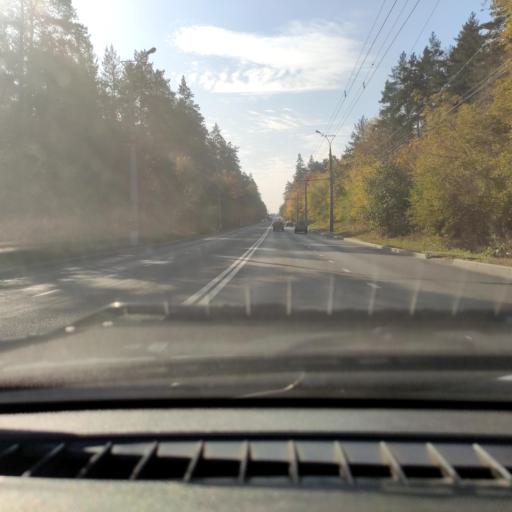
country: RU
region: Samara
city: Zhigulevsk
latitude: 53.5000
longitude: 49.4633
